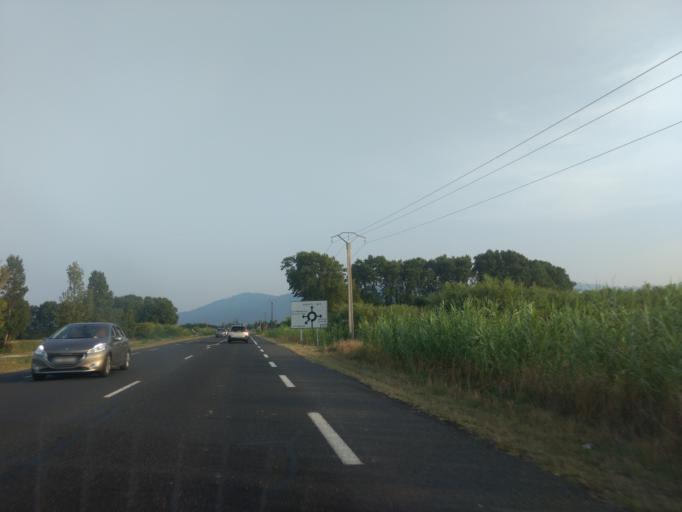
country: FR
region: Languedoc-Roussillon
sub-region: Departement des Pyrenees-Orientales
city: Latour-Bas-Elne
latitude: 42.5989
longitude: 3.0245
